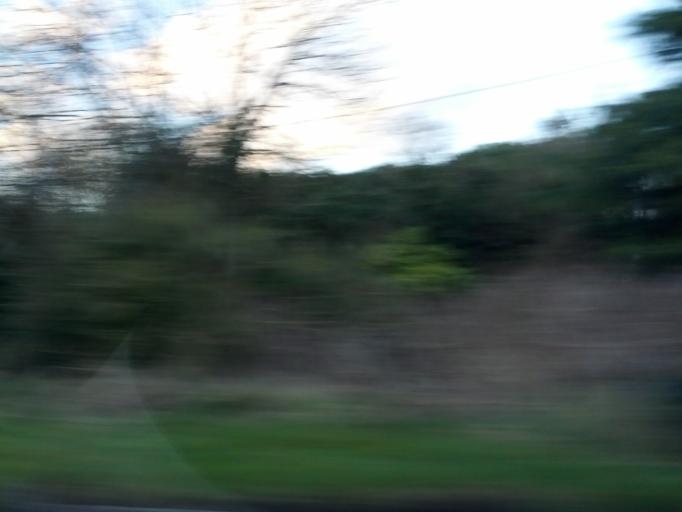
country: IE
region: Connaught
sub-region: County Galway
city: Loughrea
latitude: 53.2747
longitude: -8.6389
